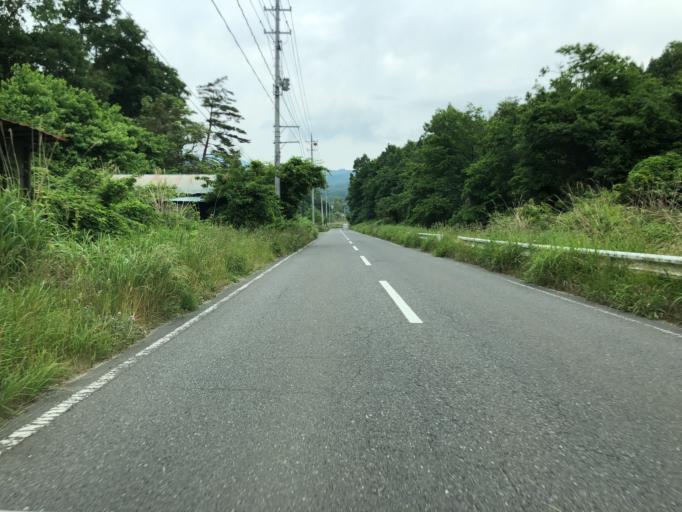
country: JP
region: Fukushima
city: Funehikimachi-funehiki
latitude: 37.4307
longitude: 140.6231
